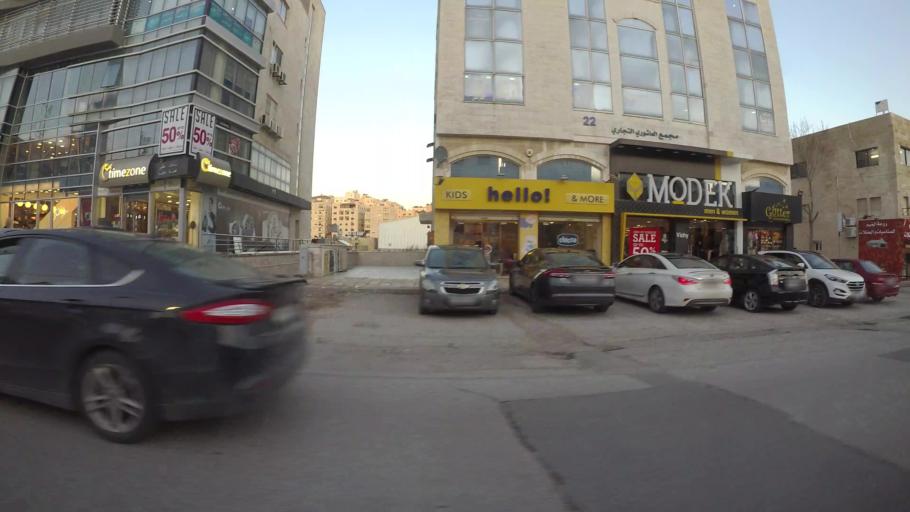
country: JO
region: Amman
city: Al Jubayhah
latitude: 31.9958
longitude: 35.8647
